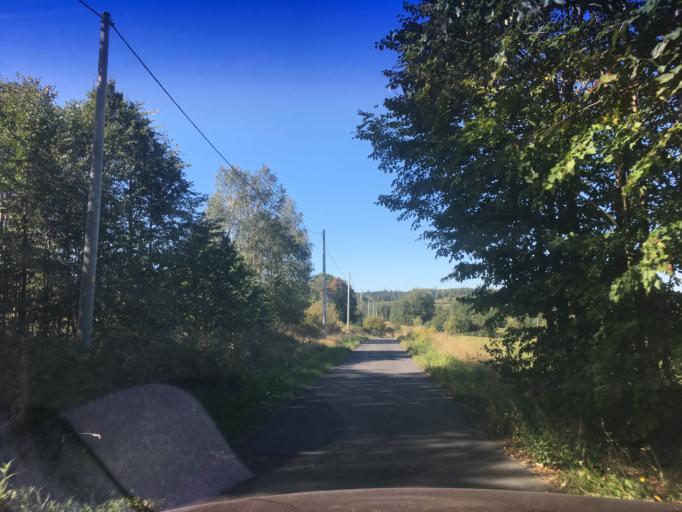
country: PL
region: Lower Silesian Voivodeship
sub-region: Powiat lubanski
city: Lesna
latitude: 50.9995
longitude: 15.1973
